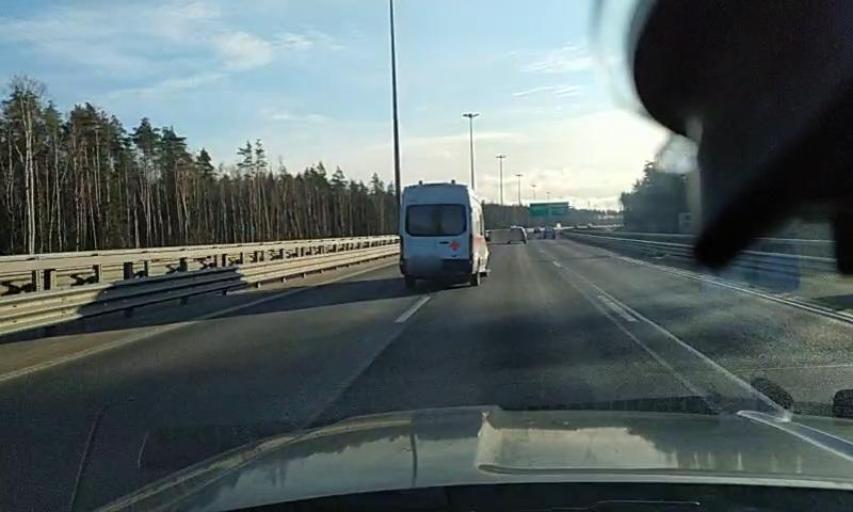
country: RU
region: St.-Petersburg
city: Pesochnyy
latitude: 60.0778
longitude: 30.1248
